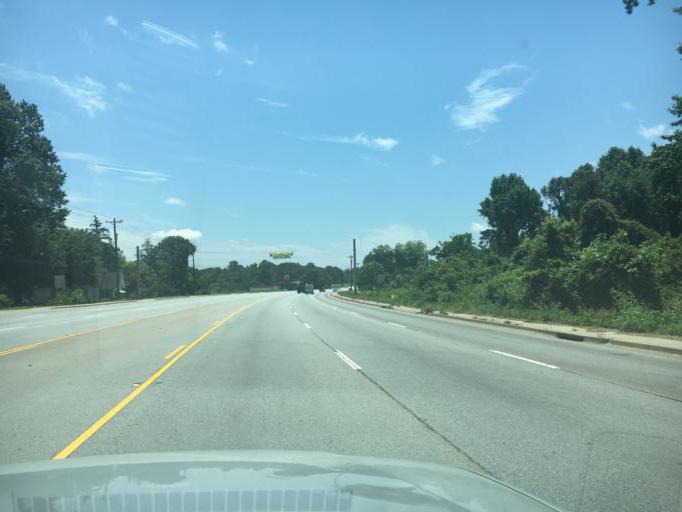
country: US
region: South Carolina
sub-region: Greenville County
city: Berea
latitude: 34.9081
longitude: -82.4608
